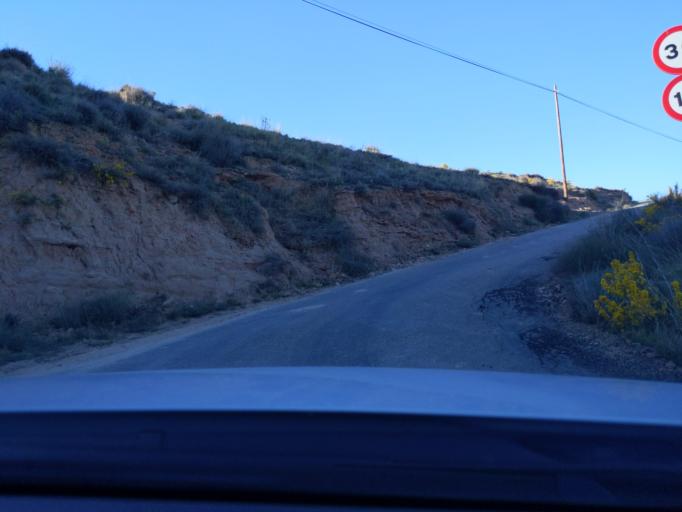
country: ES
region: La Rioja
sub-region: Provincia de La Rioja
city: Bergasa
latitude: 42.2477
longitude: -2.1374
